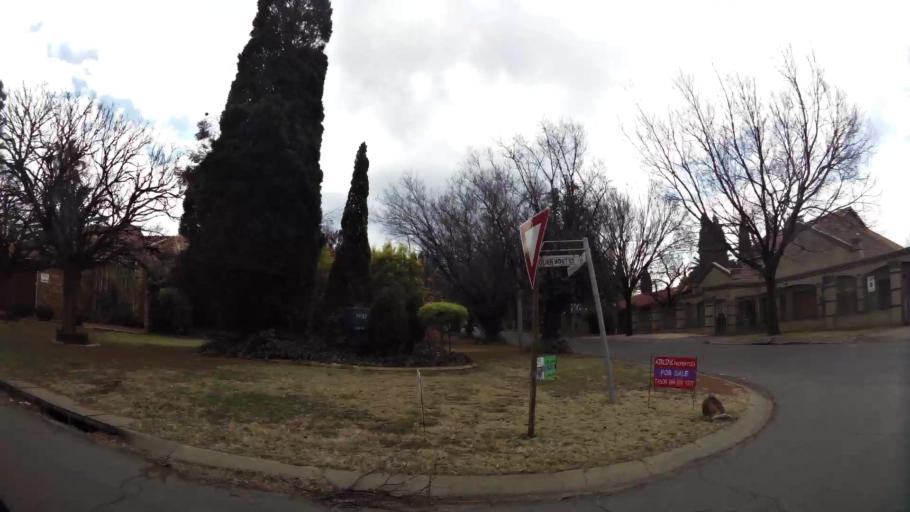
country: ZA
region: Gauteng
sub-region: Sedibeng District Municipality
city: Vanderbijlpark
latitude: -26.7356
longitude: 27.8534
